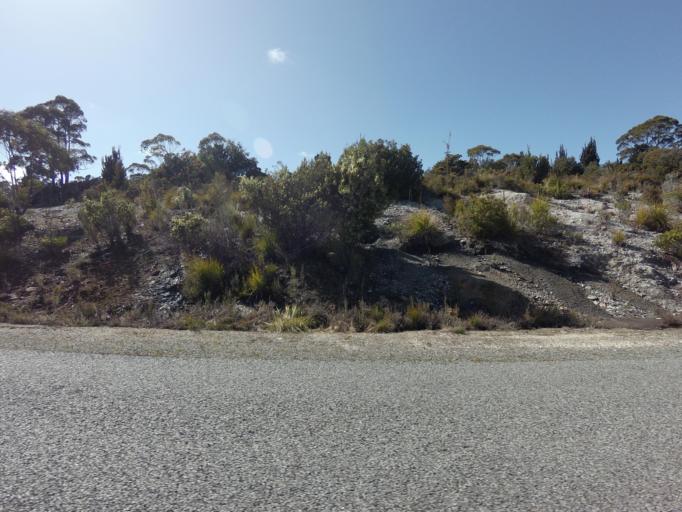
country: AU
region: Tasmania
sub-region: Derwent Valley
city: New Norfolk
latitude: -42.7609
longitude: 146.3968
